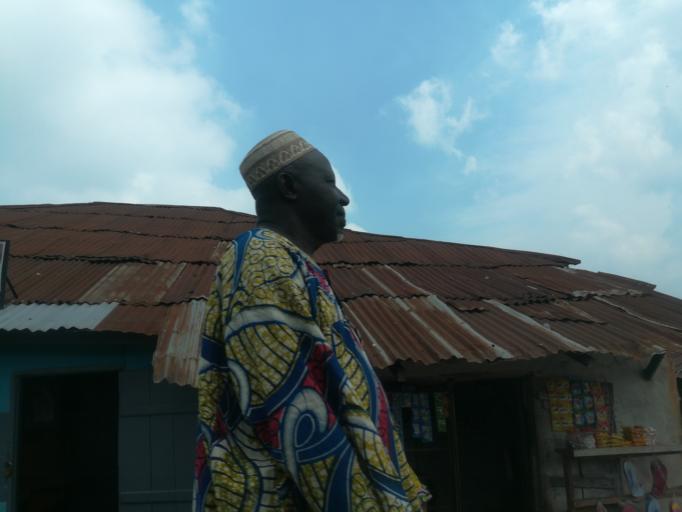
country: NG
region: Oyo
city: Ibadan
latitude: 7.3895
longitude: 3.9029
